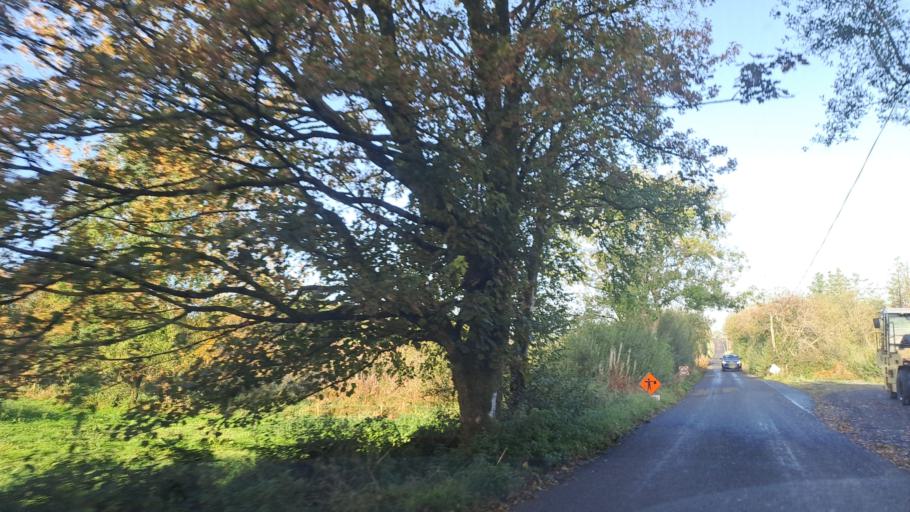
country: IE
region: Ulster
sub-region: County Monaghan
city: Castleblayney
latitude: 54.0835
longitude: -6.8554
